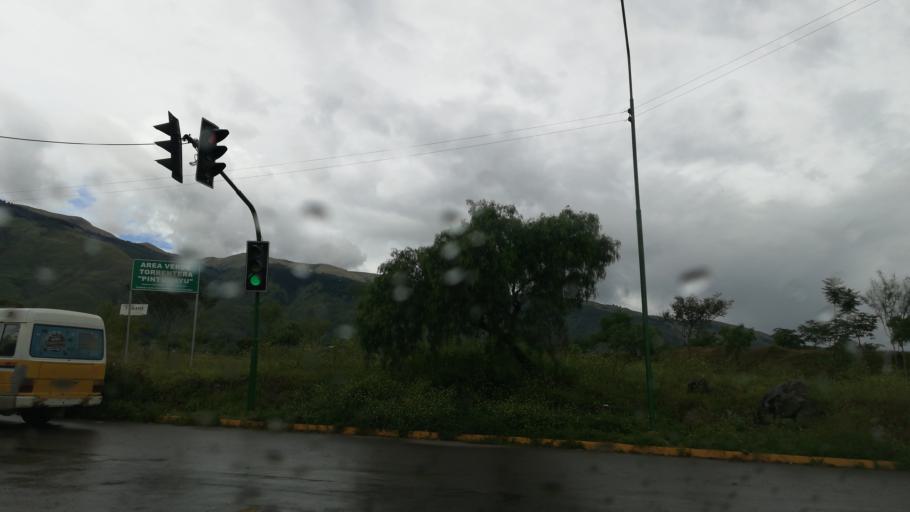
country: BO
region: Cochabamba
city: Cochabamba
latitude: -17.3515
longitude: -66.1755
